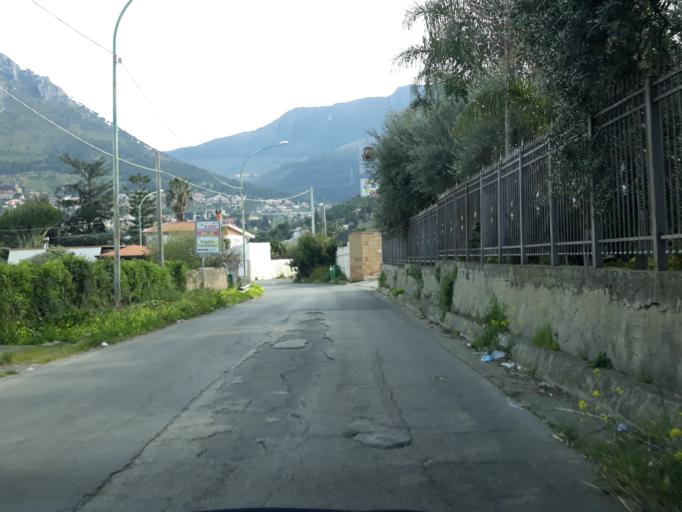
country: IT
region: Sicily
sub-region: Palermo
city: Piano Maglio-Blandino
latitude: 38.0689
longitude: 13.3051
